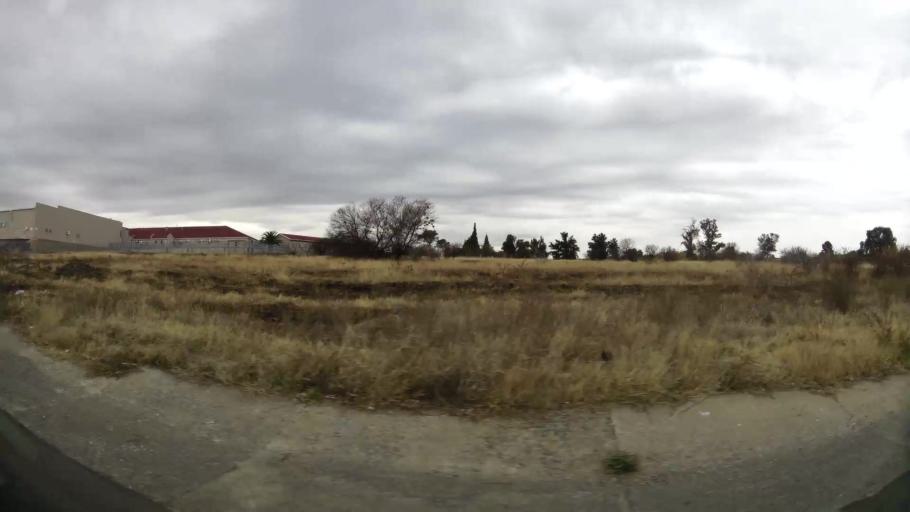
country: ZA
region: Orange Free State
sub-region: Fezile Dabi District Municipality
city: Kroonstad
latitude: -27.6492
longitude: 27.2282
